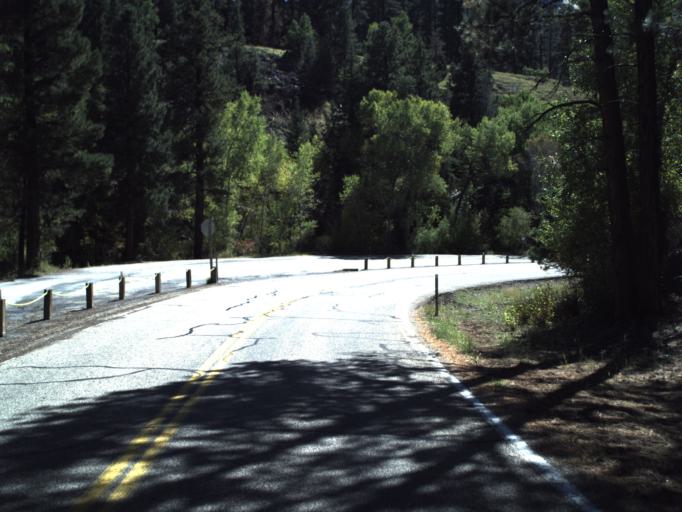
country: US
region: Utah
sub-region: Beaver County
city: Beaver
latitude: 38.2643
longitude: -112.4917
